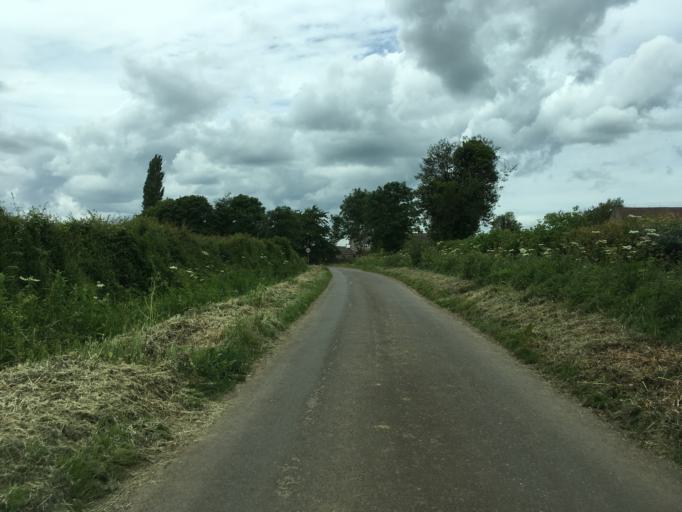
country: GB
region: England
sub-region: Wiltshire
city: Nettleton
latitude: 51.5188
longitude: -2.2406
